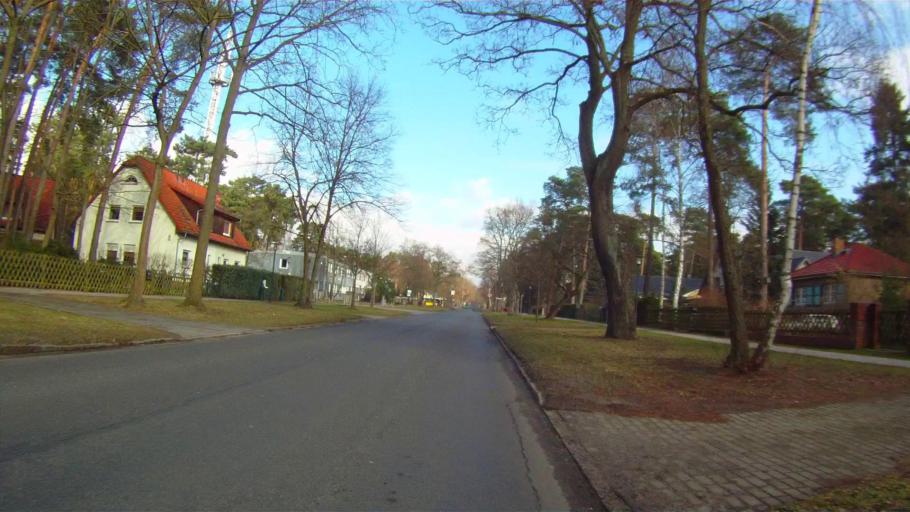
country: DE
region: Berlin
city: Mahlsdorf
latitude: 52.4833
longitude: 13.6272
